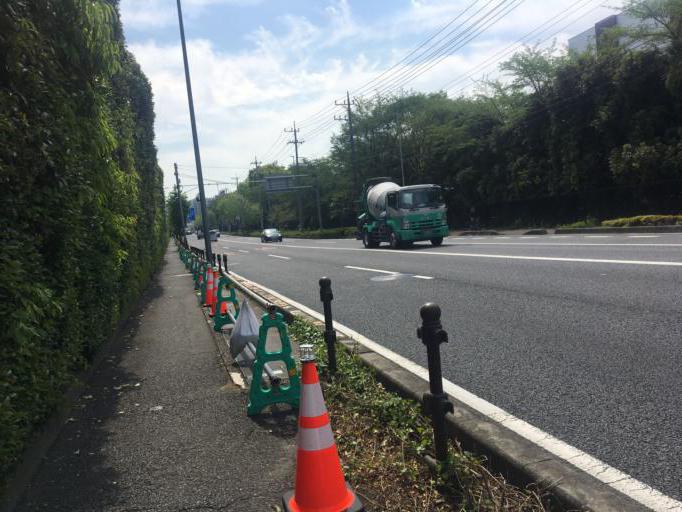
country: JP
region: Saitama
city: Wako
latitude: 35.7809
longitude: 139.6148
